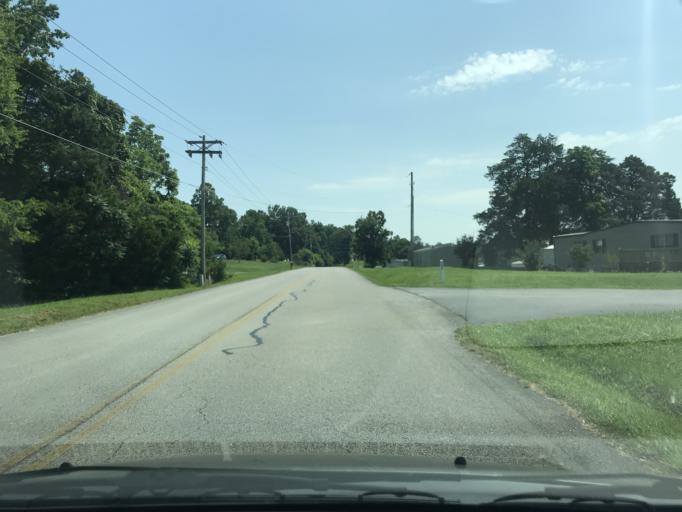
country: US
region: Tennessee
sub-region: Loudon County
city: Lenoir City
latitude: 35.8308
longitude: -84.3123
